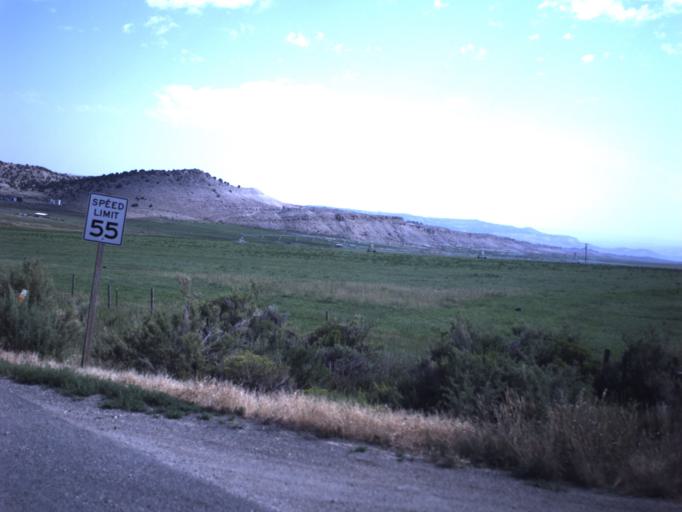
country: US
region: Utah
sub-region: Daggett County
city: Manila
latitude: 40.9451
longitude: -109.7105
